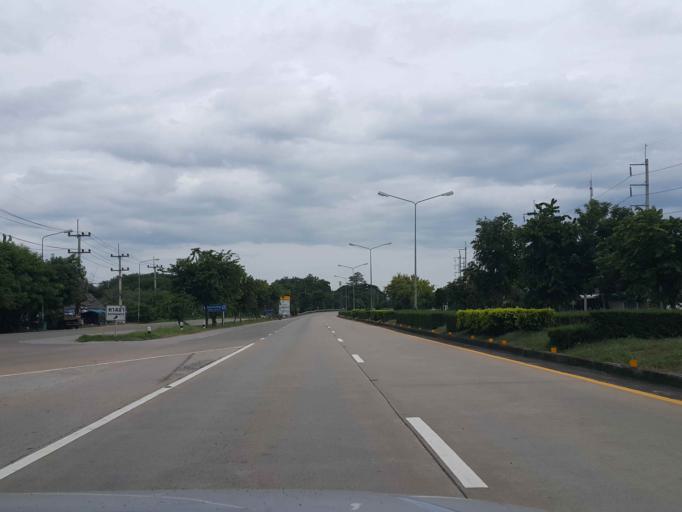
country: TH
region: Lampang
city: Lampang
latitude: 18.2730
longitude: 99.4603
